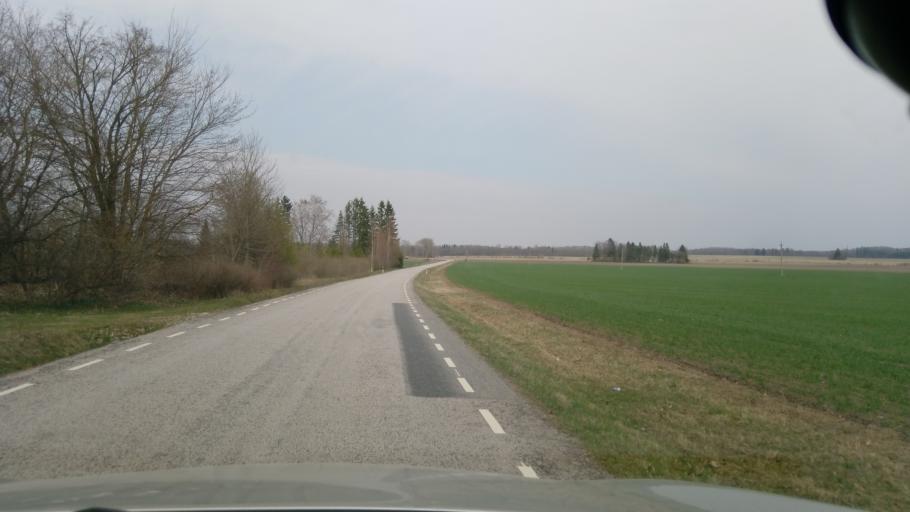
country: EE
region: Jaervamaa
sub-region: Tueri vald
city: Sarevere
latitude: 58.7877
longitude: 25.4744
